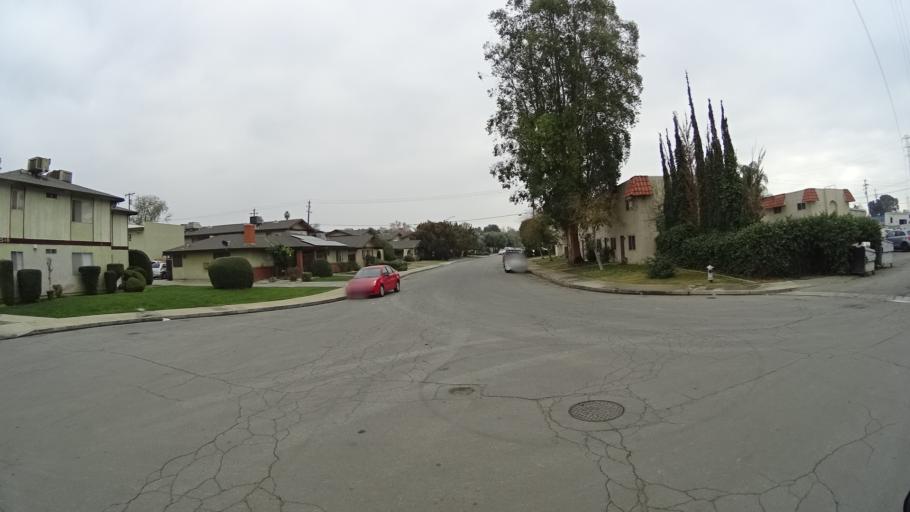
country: US
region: California
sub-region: Kern County
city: Bakersfield
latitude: 35.3829
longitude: -119.0376
